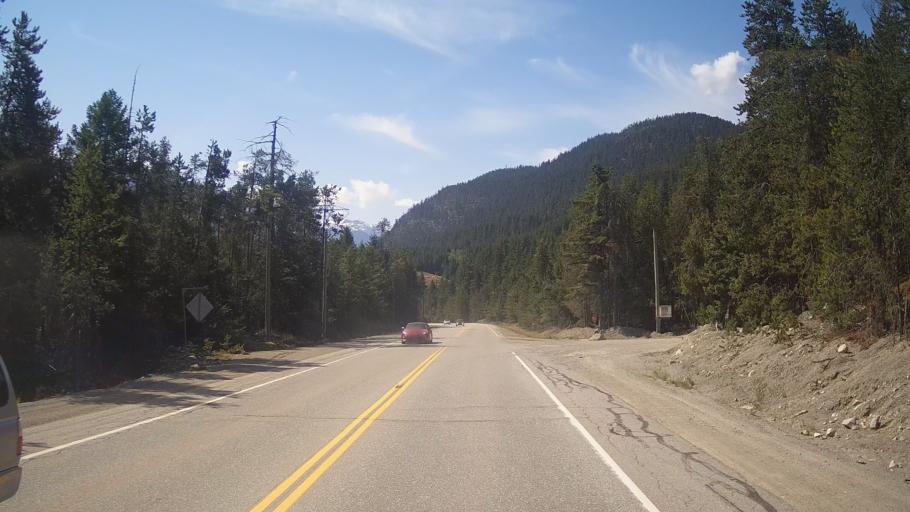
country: CA
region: British Columbia
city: Pemberton
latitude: 50.2695
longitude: -122.8673
